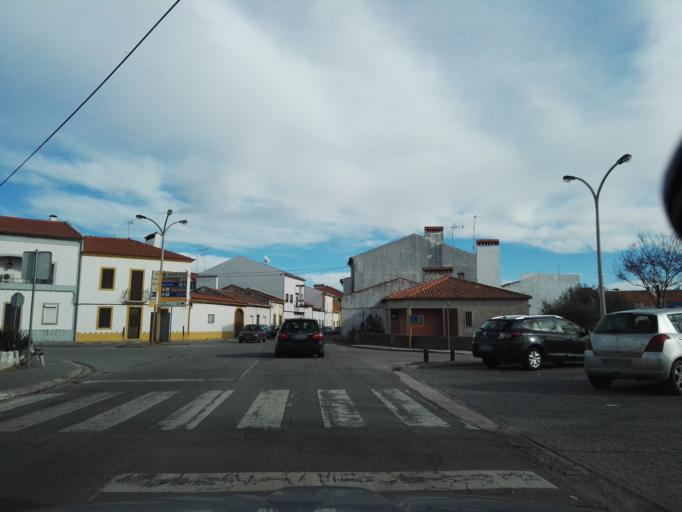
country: PT
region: Portalegre
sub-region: Nisa
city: Nisa
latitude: 39.5146
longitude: -7.6536
